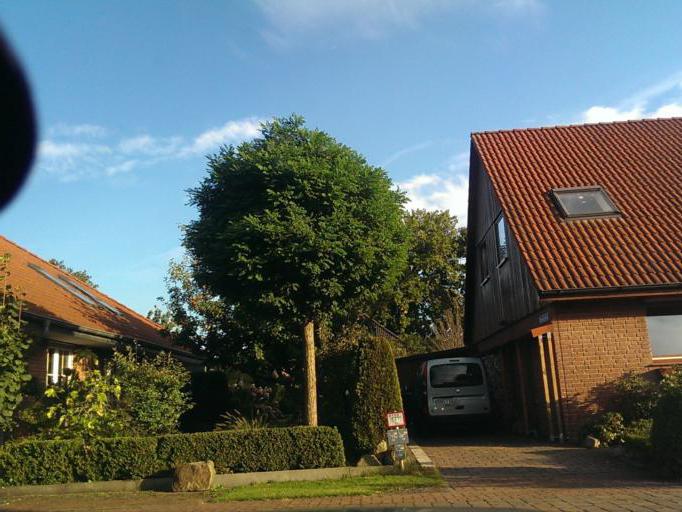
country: DE
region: Lower Saxony
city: Elze
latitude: 52.5859
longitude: 9.7321
